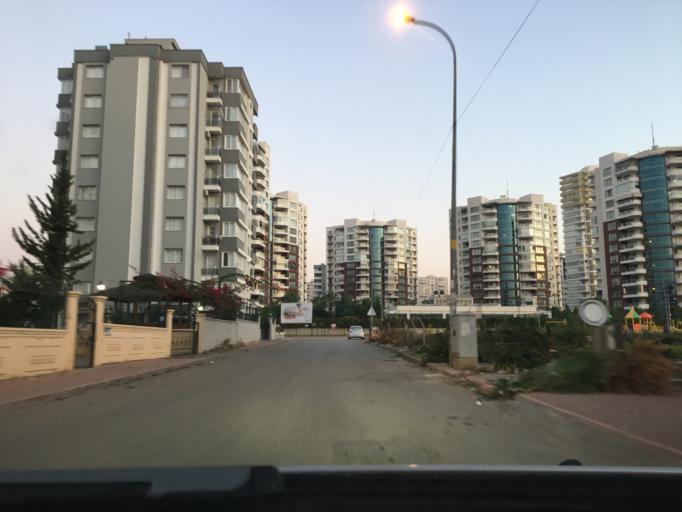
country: TR
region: Adana
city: Seyhan
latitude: 37.0197
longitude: 35.2798
